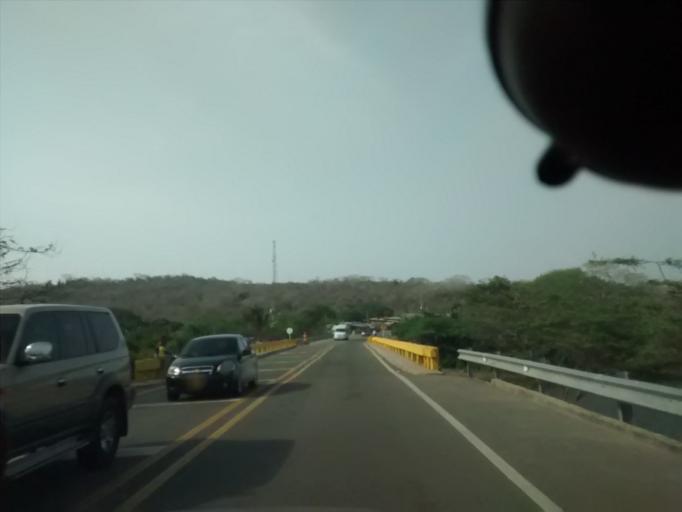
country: CO
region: Bolivar
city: Santa Catalina
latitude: 10.7386
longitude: -75.2606
